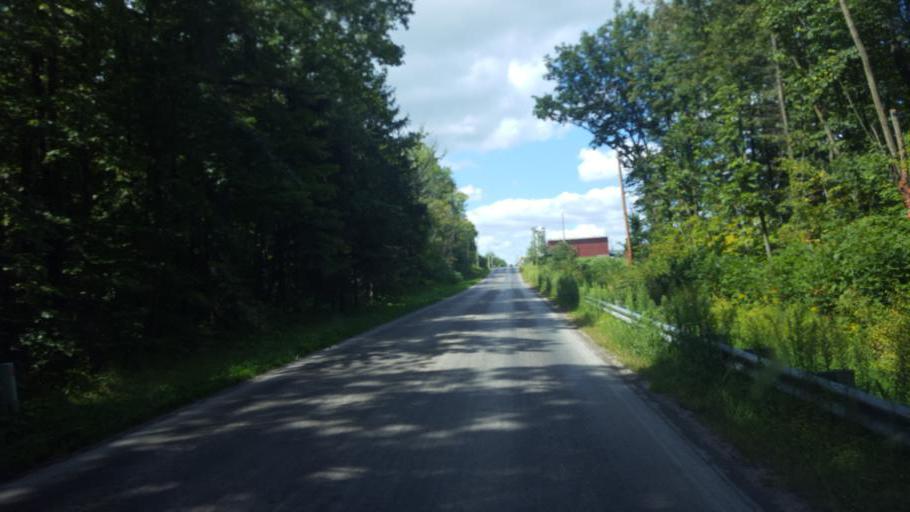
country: US
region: Ohio
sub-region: Wayne County
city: West Salem
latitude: 40.9921
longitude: -82.1727
